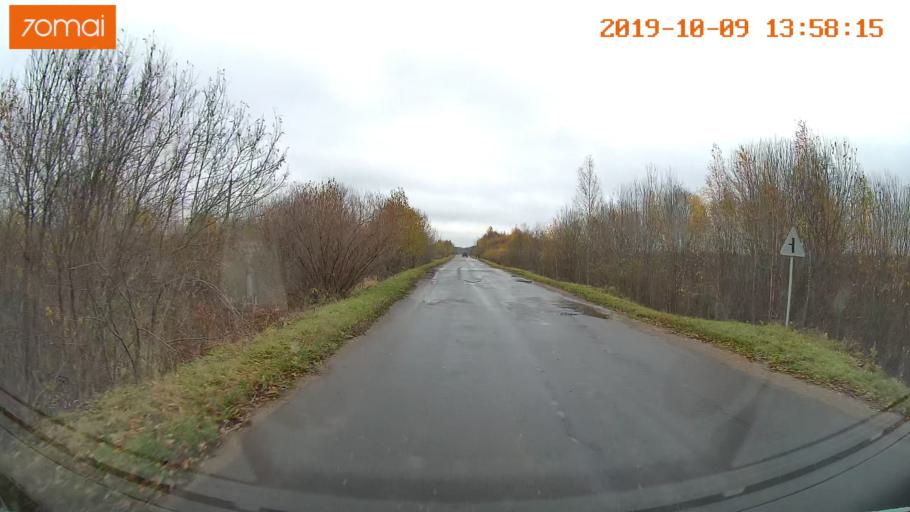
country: RU
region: Kostroma
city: Buy
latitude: 58.4328
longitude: 41.3061
